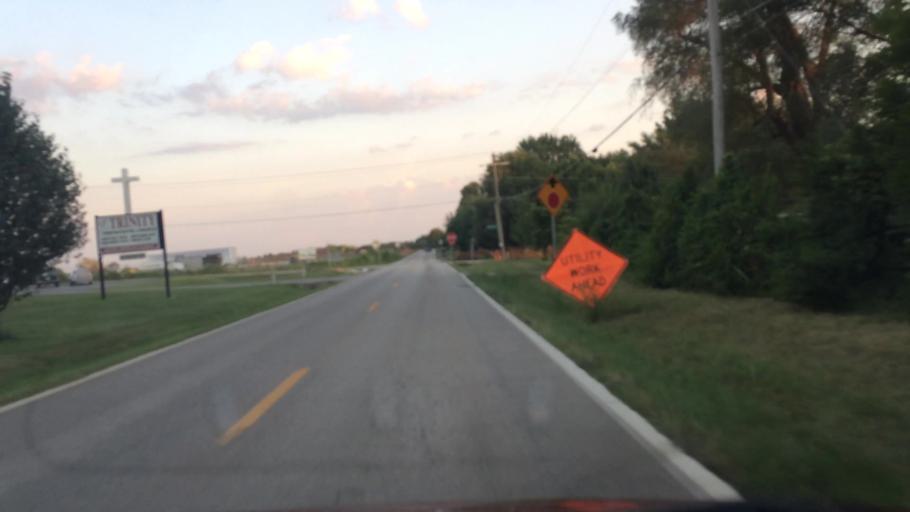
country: US
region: Missouri
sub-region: Greene County
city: Springfield
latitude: 37.2060
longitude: -93.3742
